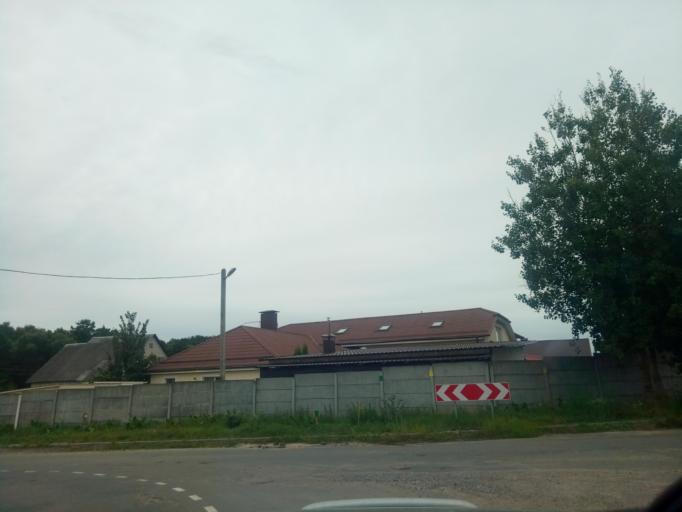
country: BY
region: Minsk
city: Zhdanovichy
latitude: 53.9243
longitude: 27.3839
